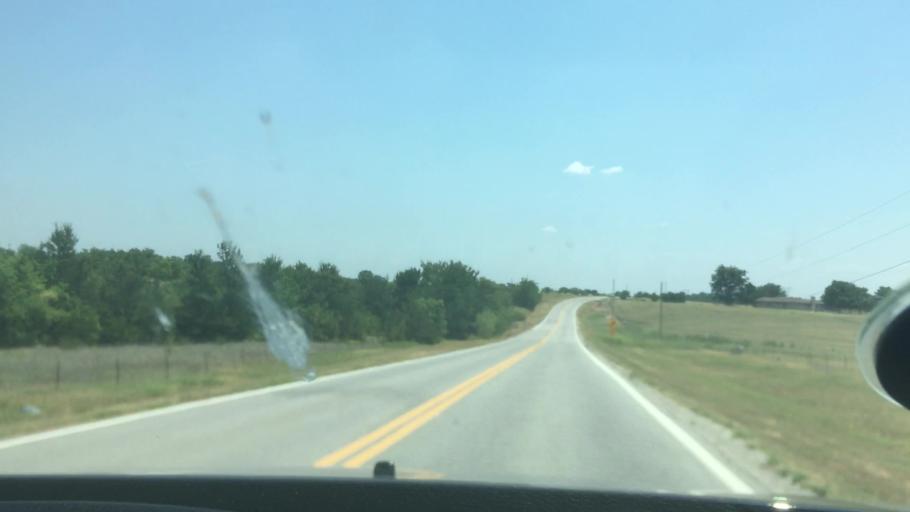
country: US
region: Oklahoma
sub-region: Bryan County
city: Durant
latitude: 34.1153
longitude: -96.3687
